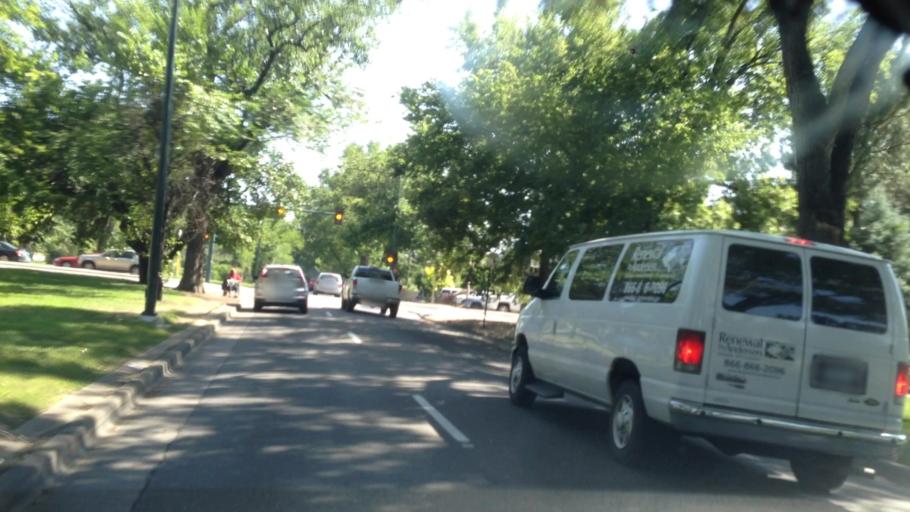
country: US
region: Colorado
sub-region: Arapahoe County
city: Glendale
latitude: 39.7407
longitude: -104.9128
